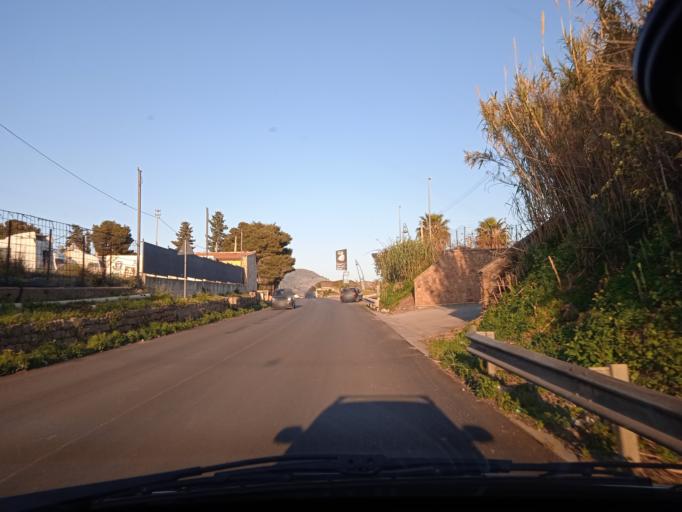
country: IT
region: Sicily
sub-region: Palermo
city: Ficarazzi
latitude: 38.0915
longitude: 13.4804
